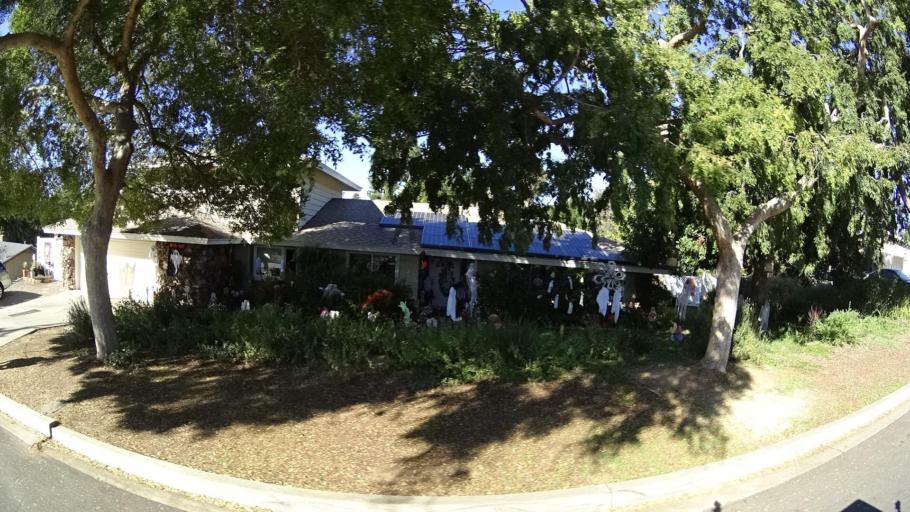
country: US
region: California
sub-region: San Diego County
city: Bonita
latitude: 32.6816
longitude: -117.0156
